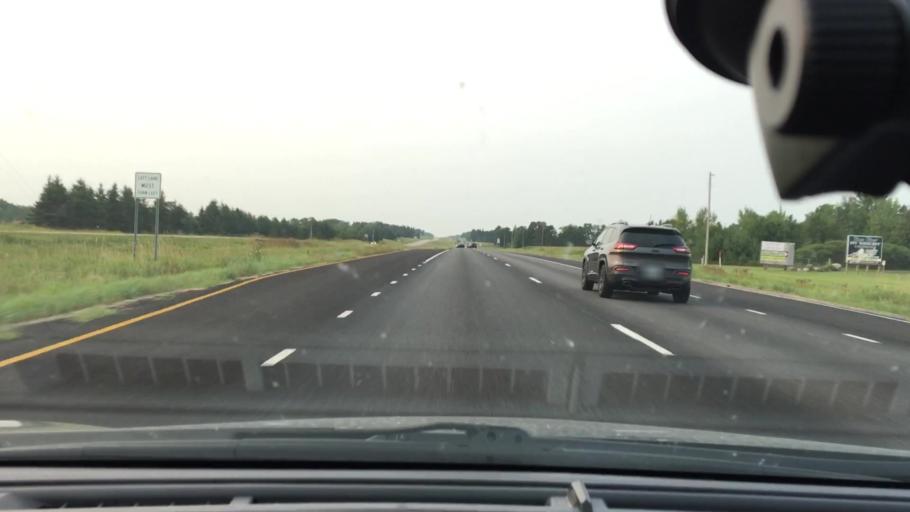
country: US
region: Minnesota
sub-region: Mille Lacs County
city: Milaca
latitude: 45.9434
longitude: -93.6625
